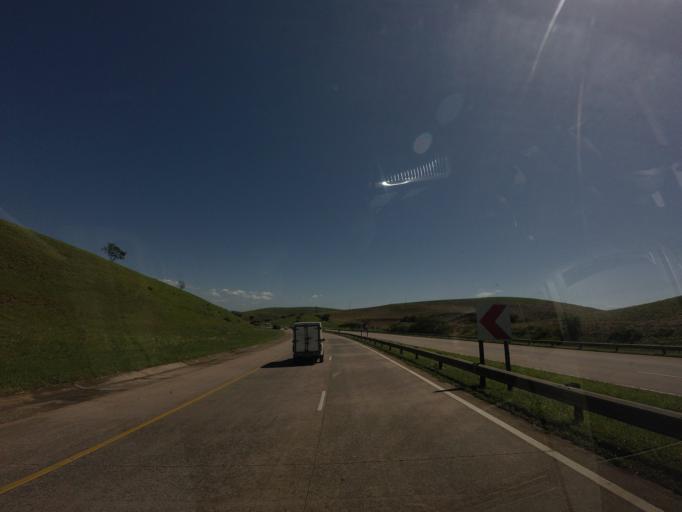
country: ZA
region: KwaZulu-Natal
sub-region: iLembe District Municipality
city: Stanger
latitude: -29.3868
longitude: 31.2974
